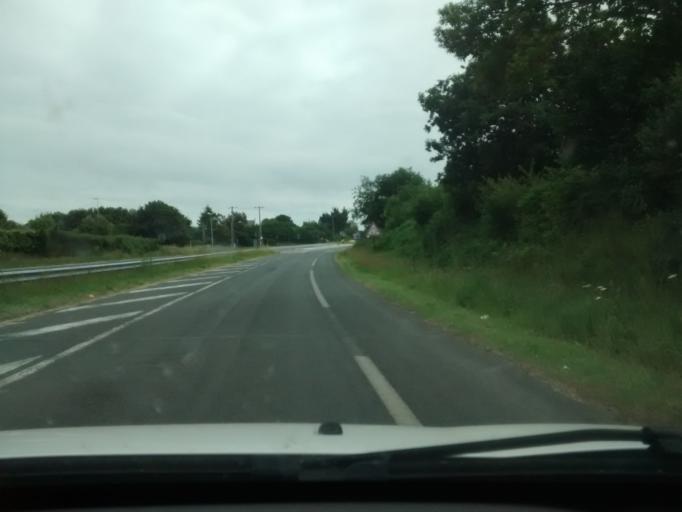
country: FR
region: Brittany
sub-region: Departement des Cotes-d'Armor
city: Saint-Quay-Perros
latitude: 48.7754
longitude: -3.4463
